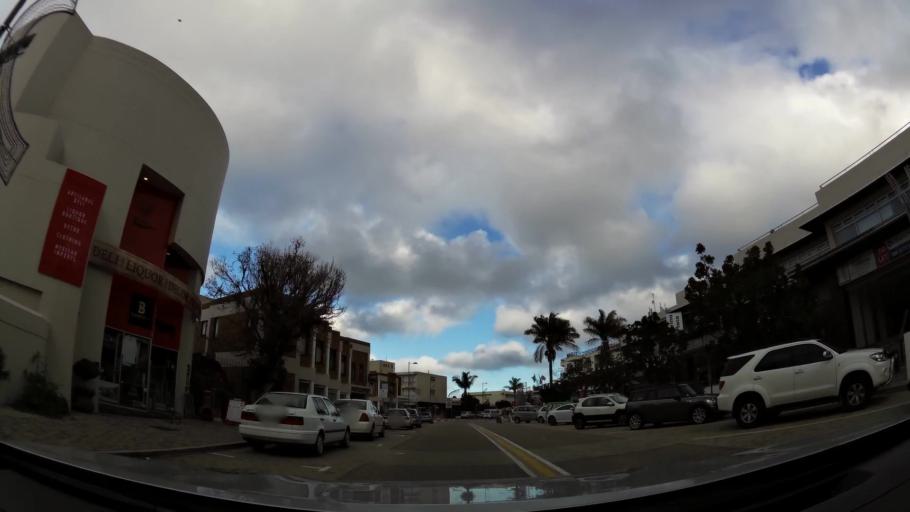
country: ZA
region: Western Cape
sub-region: Eden District Municipality
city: Plettenberg Bay
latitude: -34.0524
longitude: 23.3721
